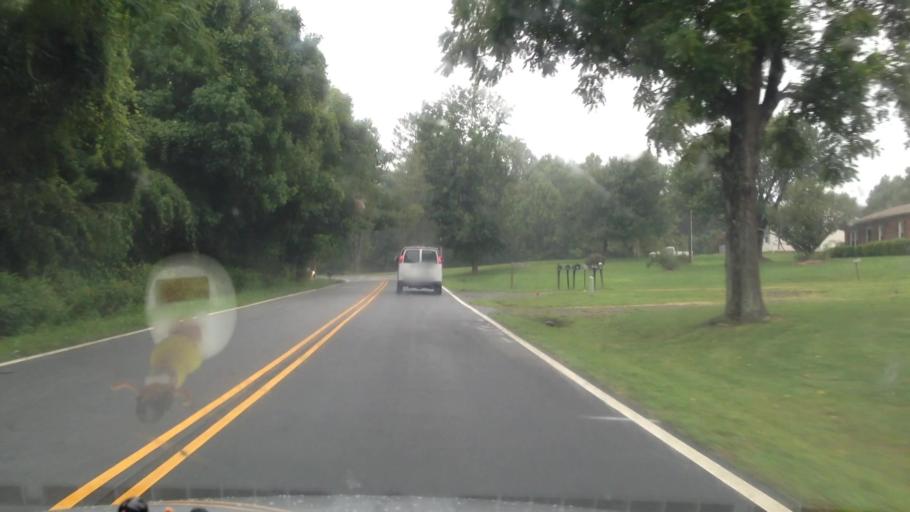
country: US
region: North Carolina
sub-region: Forsyth County
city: Kernersville
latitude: 36.1541
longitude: -80.0954
